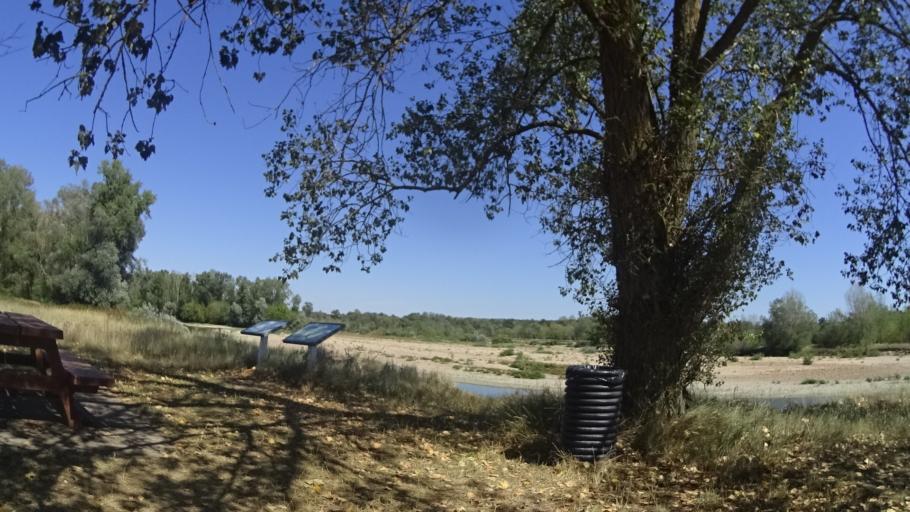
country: FR
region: Centre
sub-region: Departement du Loiret
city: Bonny-sur-Loire
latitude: 47.5350
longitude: 2.8477
